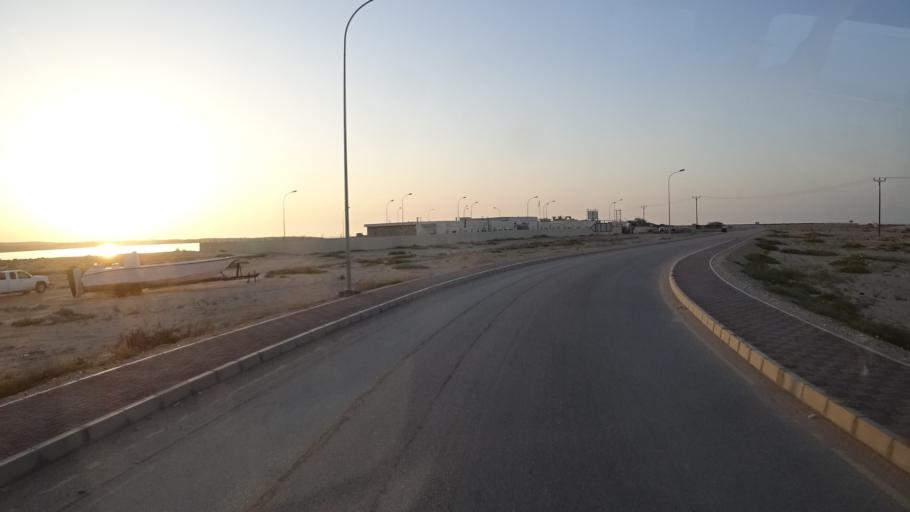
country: OM
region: Ash Sharqiyah
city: Sur
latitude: 22.5280
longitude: 59.7644
